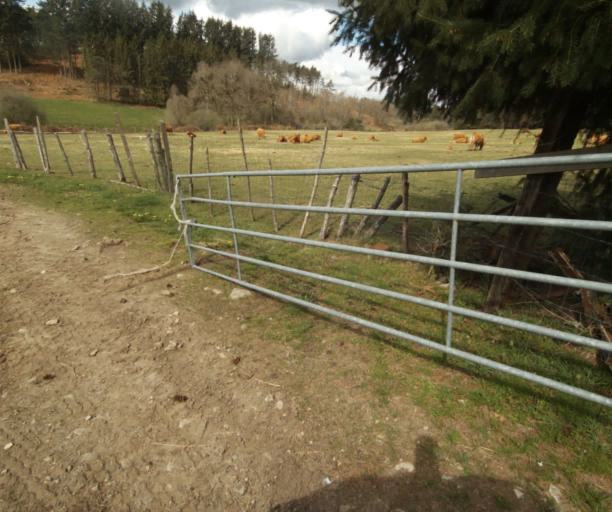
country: FR
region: Limousin
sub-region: Departement de la Correze
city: Correze
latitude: 45.3895
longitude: 1.9129
